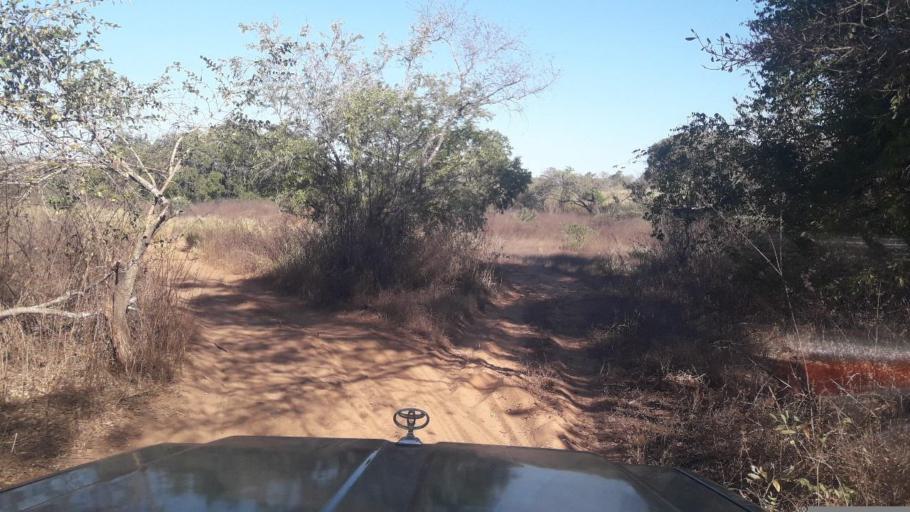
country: MG
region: Boeny
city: Sitampiky
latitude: -16.4230
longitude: 45.6193
